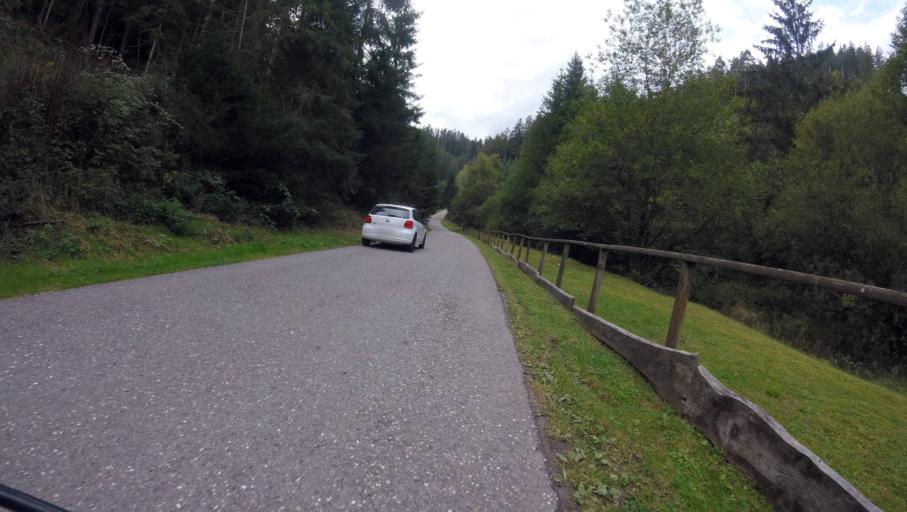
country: DE
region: Baden-Wuerttemberg
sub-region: Karlsruhe Region
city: Grombach
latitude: 48.5915
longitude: 8.5297
